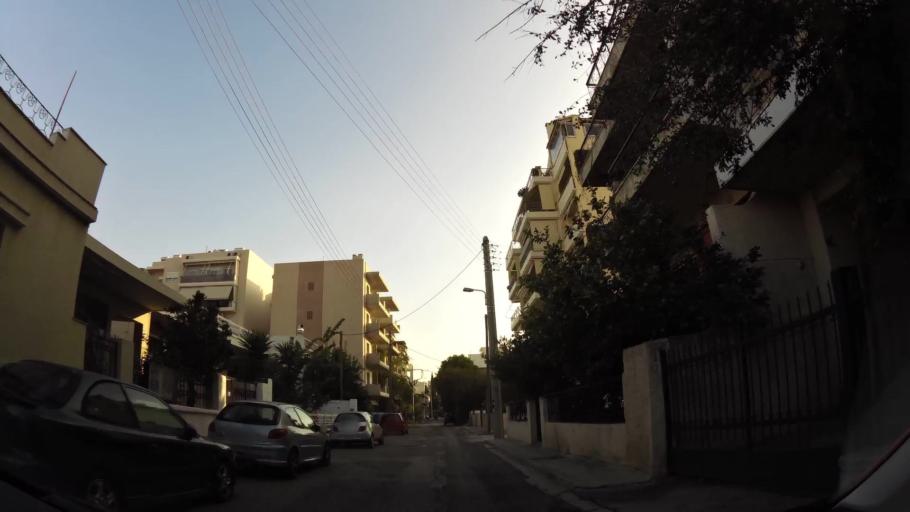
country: GR
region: Attica
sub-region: Nomarchia Anatolikis Attikis
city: Acharnes
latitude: 38.0817
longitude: 23.7429
